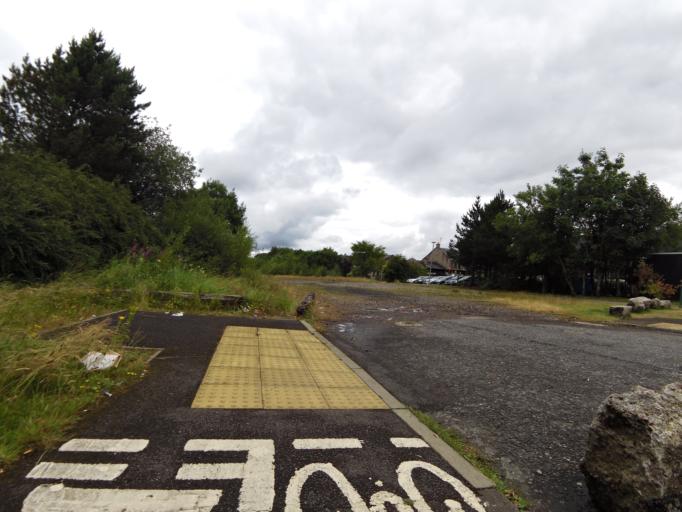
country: GB
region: Scotland
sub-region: Highland
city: Fort William
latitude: 56.8224
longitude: -5.1062
